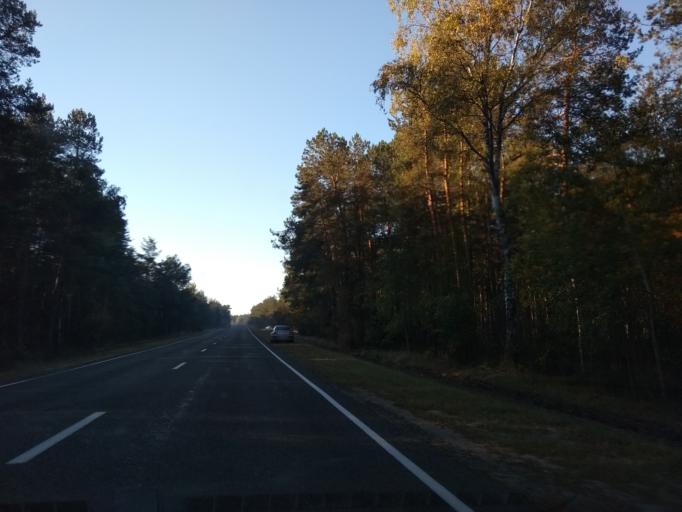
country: BY
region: Brest
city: Kobryn
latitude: 52.1044
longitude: 24.2811
